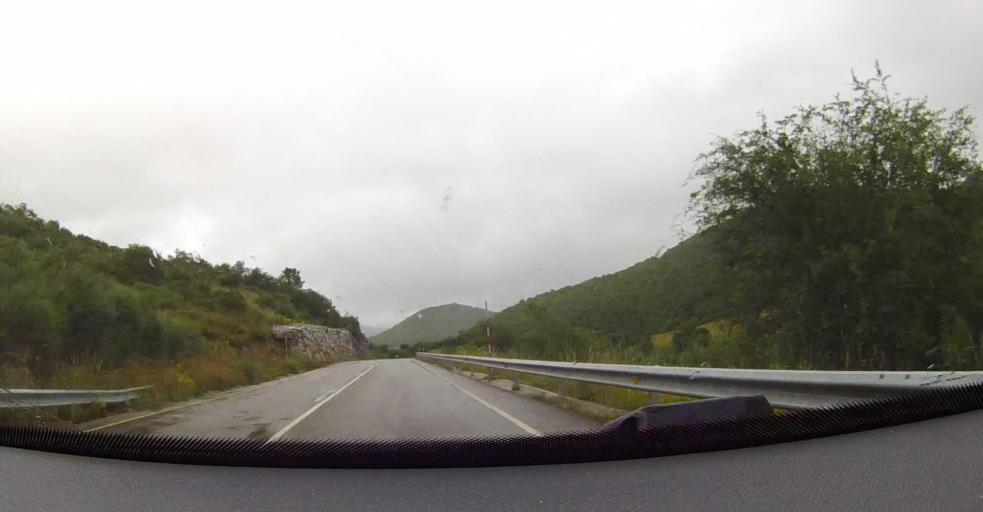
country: ES
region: Castille and Leon
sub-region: Provincia de Leon
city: Marana
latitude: 43.0693
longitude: -5.1752
